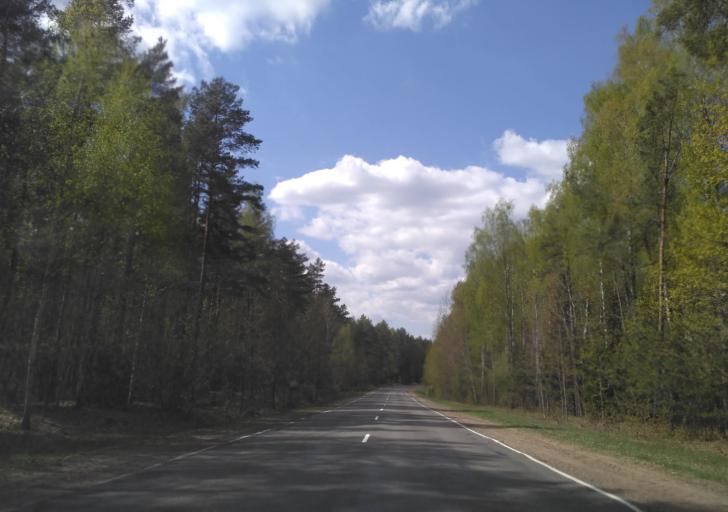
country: BY
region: Minsk
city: Vilyeyka
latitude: 54.4987
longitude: 27.0964
